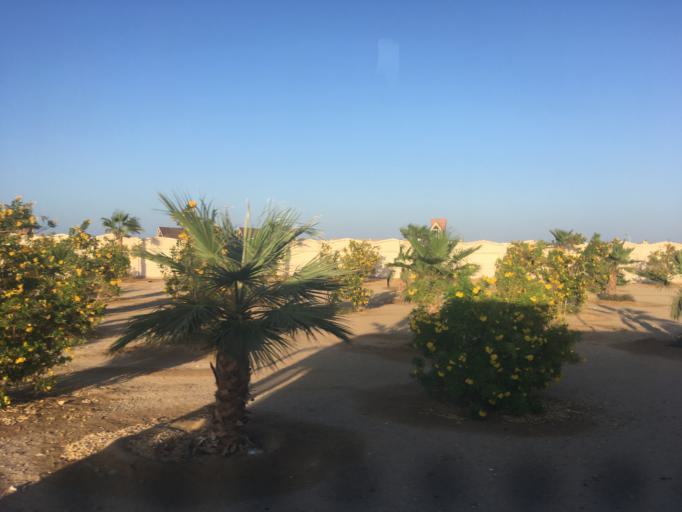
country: EG
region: Red Sea
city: Al Qusayr
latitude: 25.9643
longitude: 34.3596
